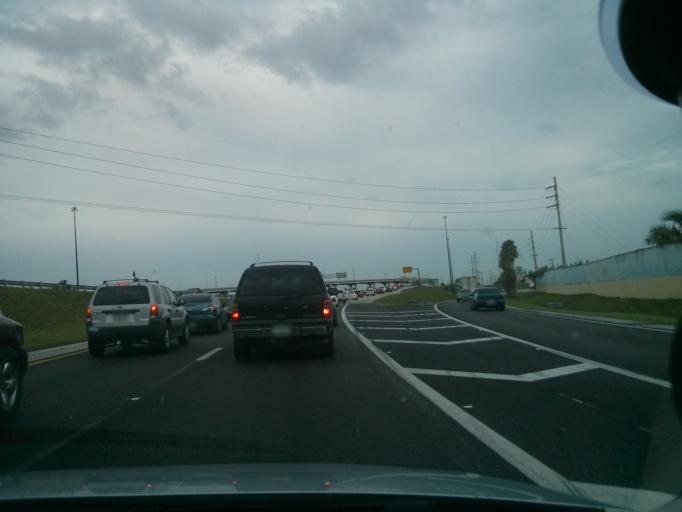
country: US
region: Florida
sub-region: Miami-Dade County
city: Norland
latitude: 25.9314
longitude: -80.2128
